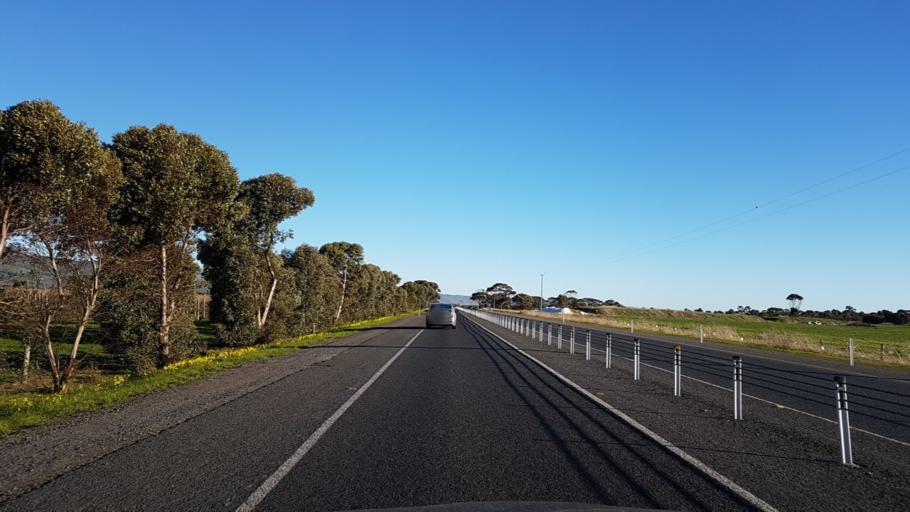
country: AU
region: South Australia
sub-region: Onkaparinga
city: Aldinga
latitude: -35.2574
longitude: 138.4923
